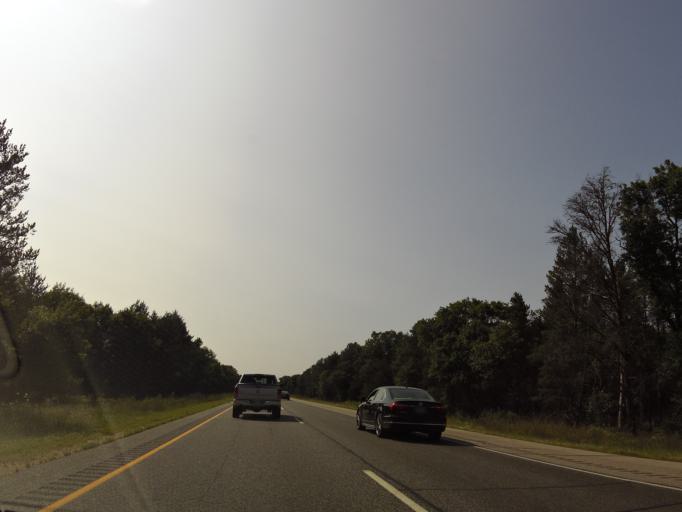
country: US
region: Wisconsin
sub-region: Monroe County
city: Sparta
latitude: 43.9414
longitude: -90.6652
